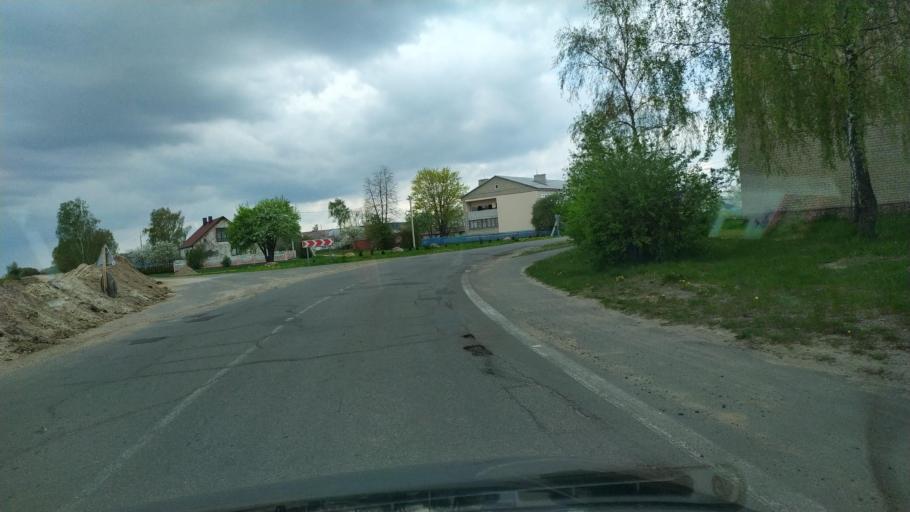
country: BY
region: Brest
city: Pruzhany
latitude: 52.5651
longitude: 24.4202
